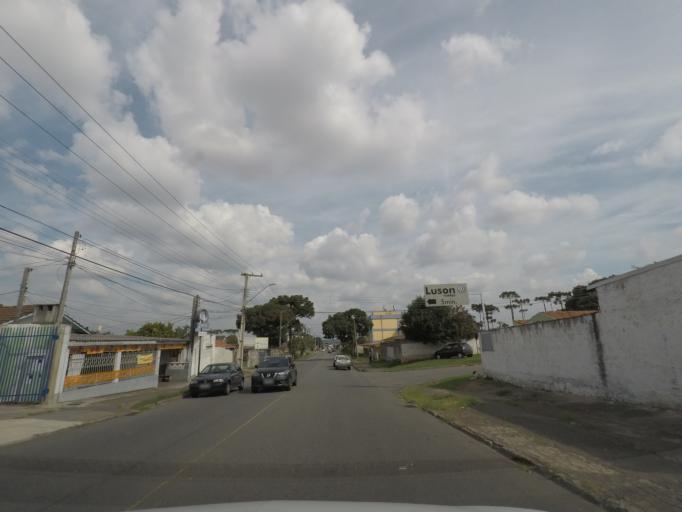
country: BR
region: Parana
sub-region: Sao Jose Dos Pinhais
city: Sao Jose dos Pinhais
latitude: -25.4894
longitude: -49.2144
